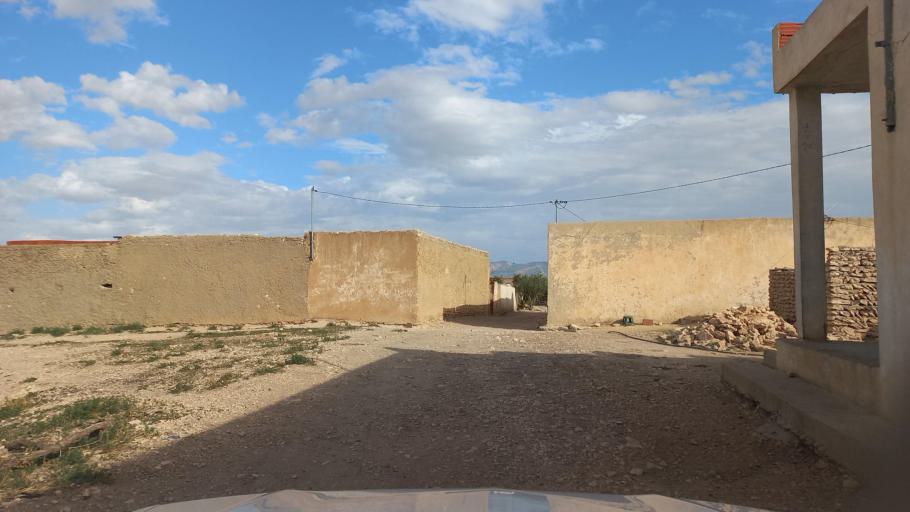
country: TN
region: Al Qasrayn
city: Sbiba
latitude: 35.4515
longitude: 9.0875
